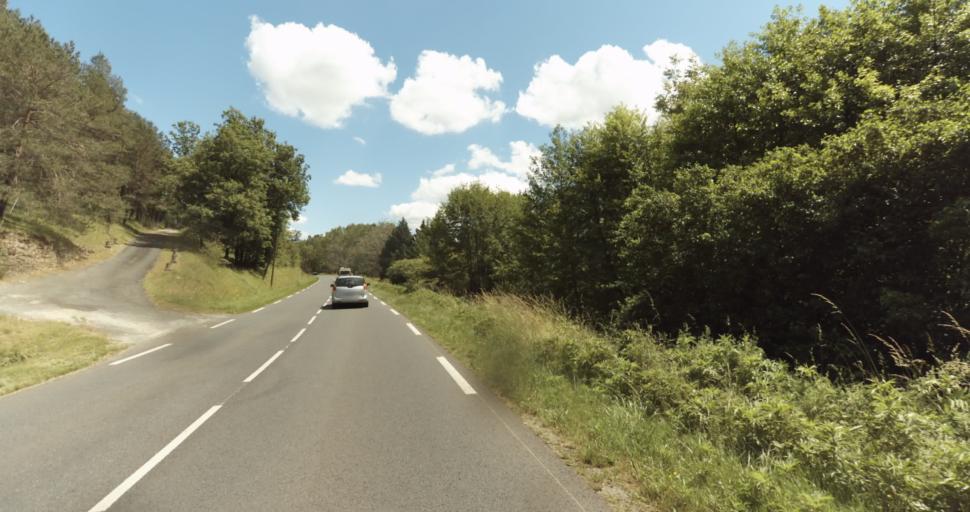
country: FR
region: Aquitaine
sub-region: Departement de la Dordogne
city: Le Bugue
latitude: 44.8423
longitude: 0.8512
